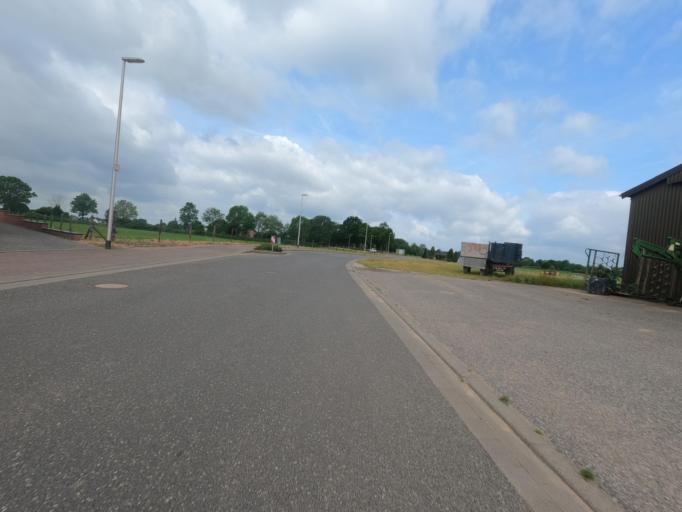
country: DE
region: North Rhine-Westphalia
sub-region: Regierungsbezirk Koln
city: Heinsberg
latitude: 51.0932
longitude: 6.1148
